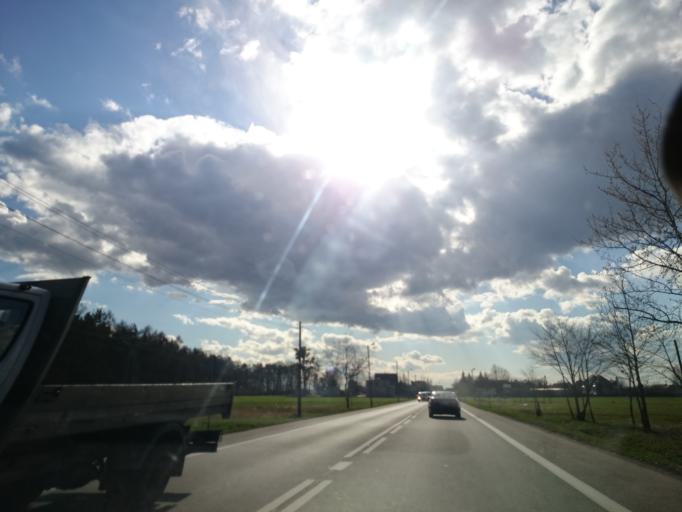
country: PL
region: Opole Voivodeship
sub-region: Powiat opolski
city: Niemodlin
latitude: 50.6535
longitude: 17.6816
